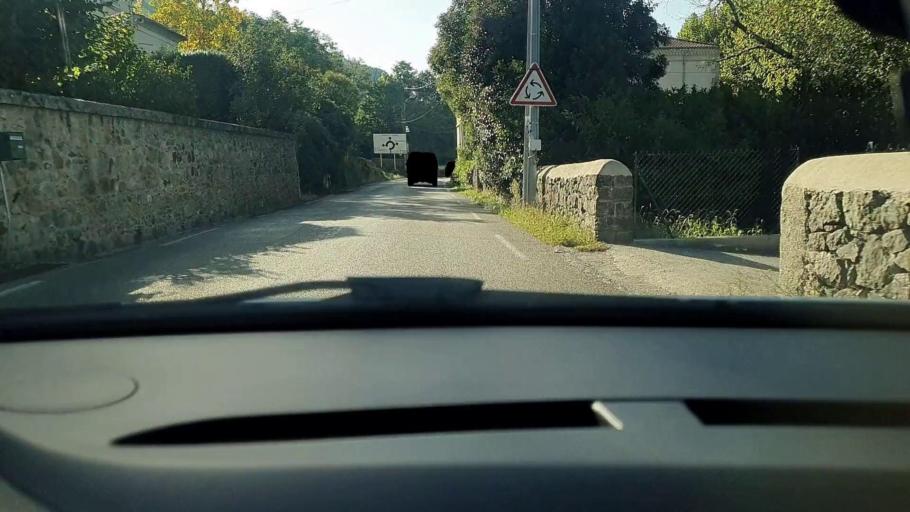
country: FR
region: Languedoc-Roussillon
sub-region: Departement du Gard
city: Besseges
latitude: 44.2857
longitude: 4.1252
